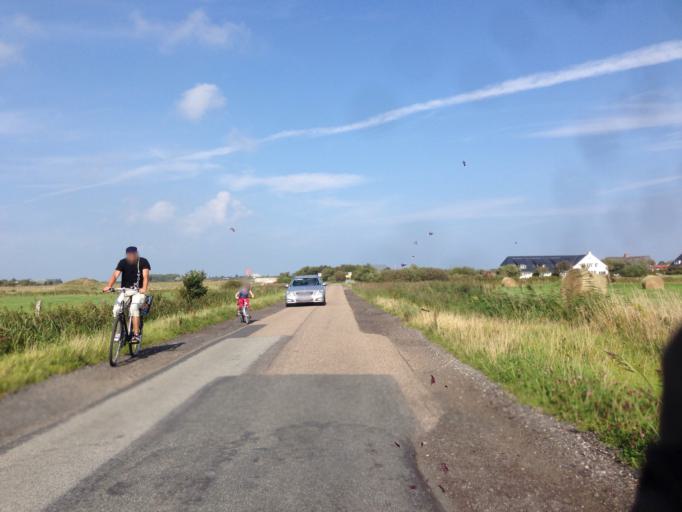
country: DE
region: Schleswig-Holstein
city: Keitum
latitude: 54.8894
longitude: 8.3537
